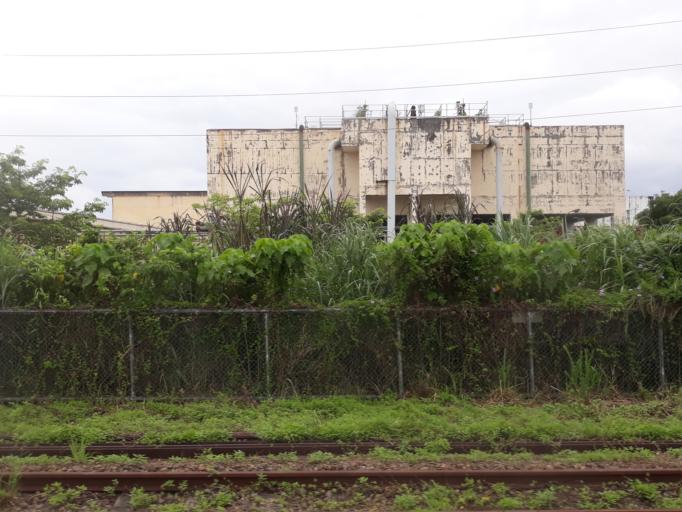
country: TW
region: Taiwan
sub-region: Yilan
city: Yilan
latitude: 24.6975
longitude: 121.7752
